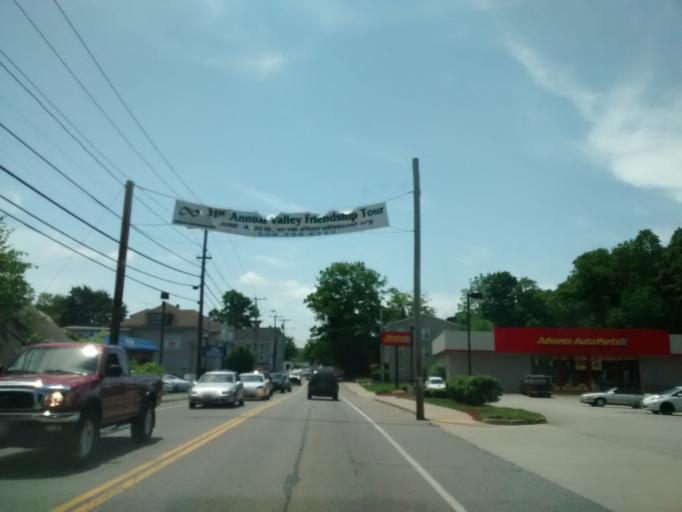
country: US
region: Massachusetts
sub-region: Worcester County
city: Whitinsville
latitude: 42.1147
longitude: -71.6546
